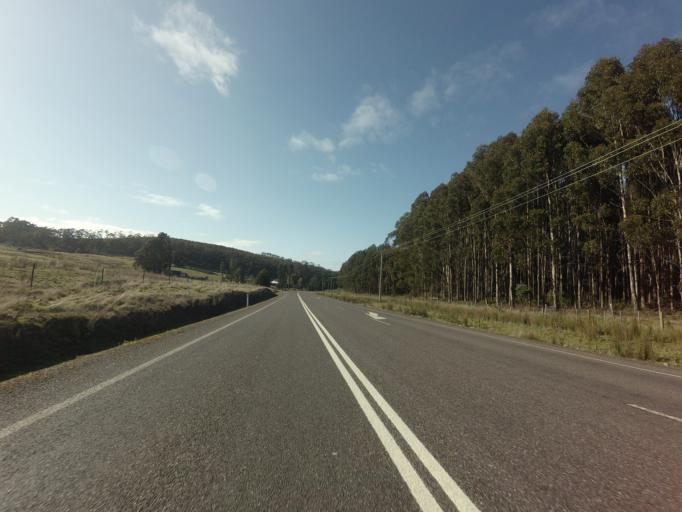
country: AU
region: Tasmania
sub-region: Huon Valley
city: Geeveston
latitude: -43.2557
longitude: 147.0008
